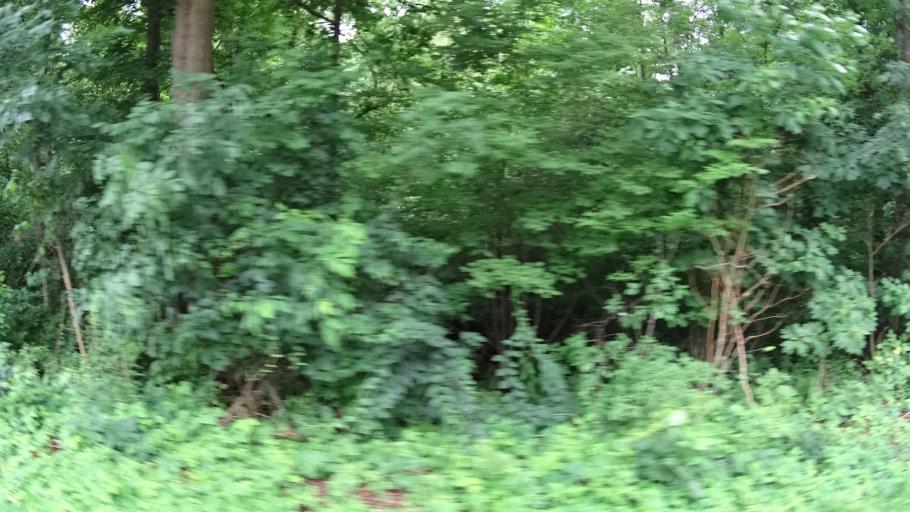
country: US
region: Ohio
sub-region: Erie County
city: Milan
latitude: 41.2855
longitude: -82.5430
